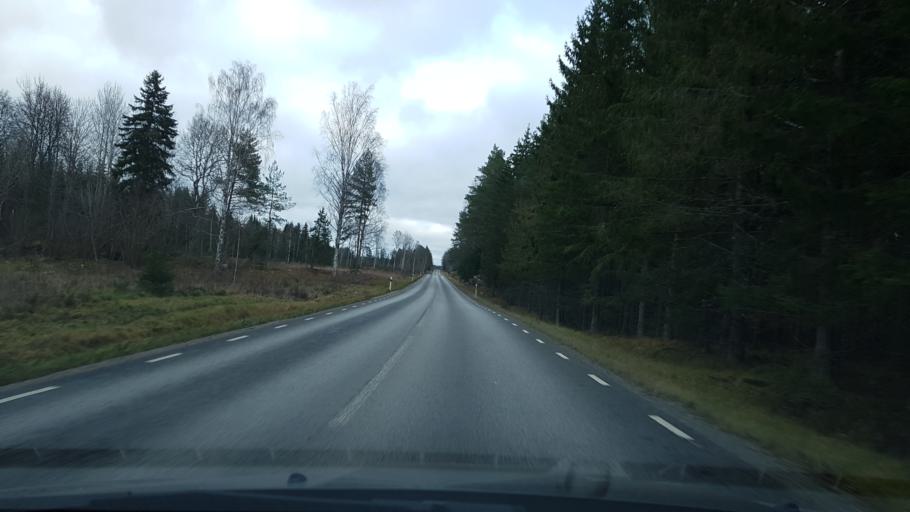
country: SE
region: Stockholm
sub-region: Norrtalje Kommun
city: Hallstavik
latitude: 60.0367
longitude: 18.5116
